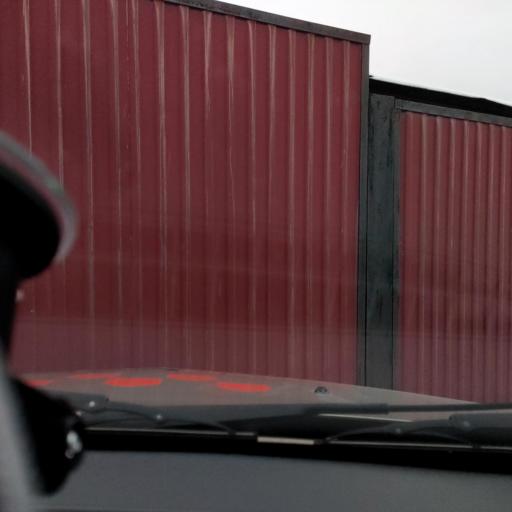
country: RU
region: Bashkortostan
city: Mikhaylovka
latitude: 54.8272
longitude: 55.9106
